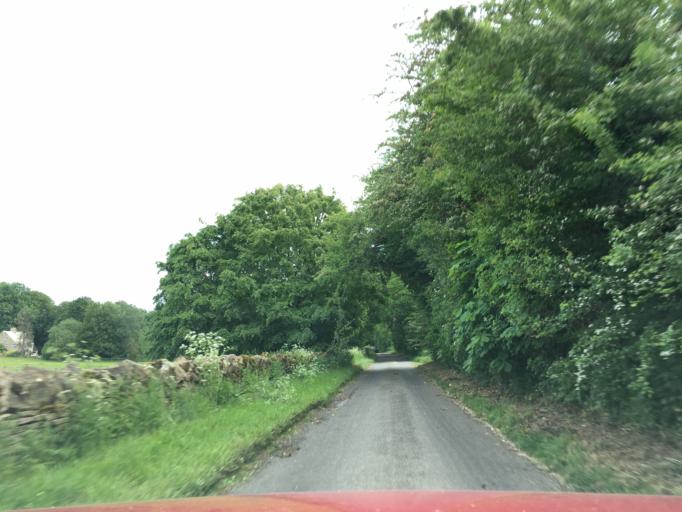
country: GB
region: England
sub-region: Gloucestershire
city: Cirencester
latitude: 51.7551
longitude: -1.9789
